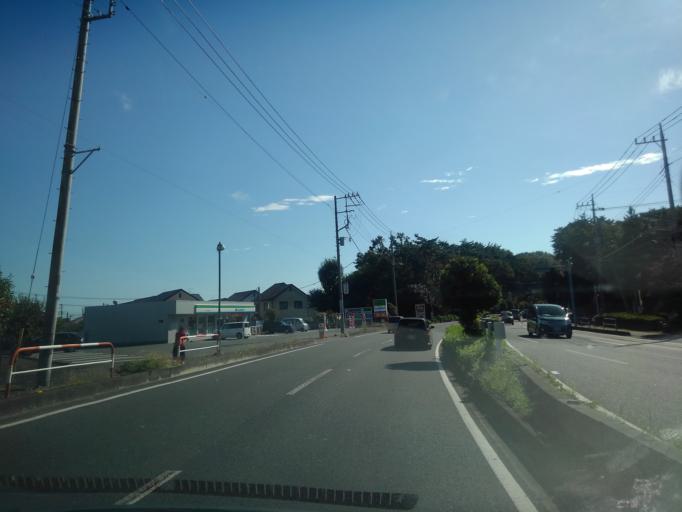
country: JP
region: Saitama
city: Sayama
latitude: 35.8223
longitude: 139.3846
